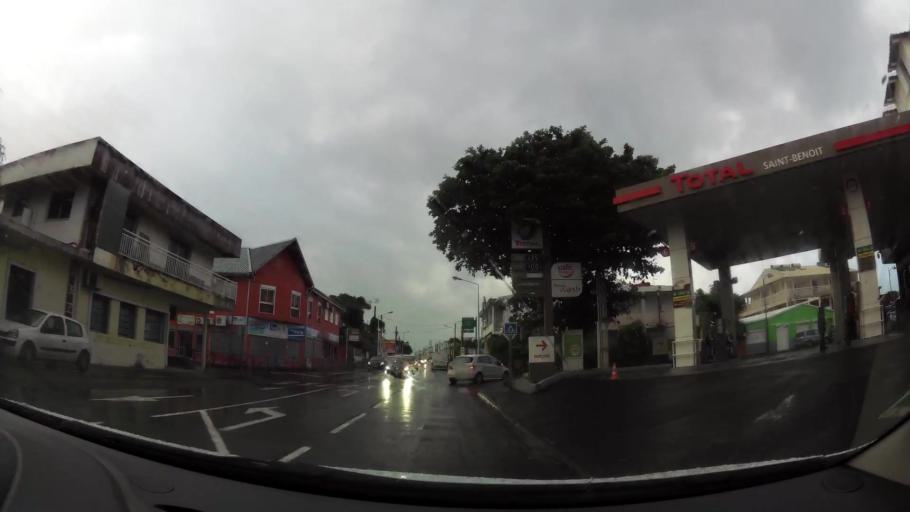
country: RE
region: Reunion
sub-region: Reunion
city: Saint-Benoit
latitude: -21.0380
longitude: 55.7172
